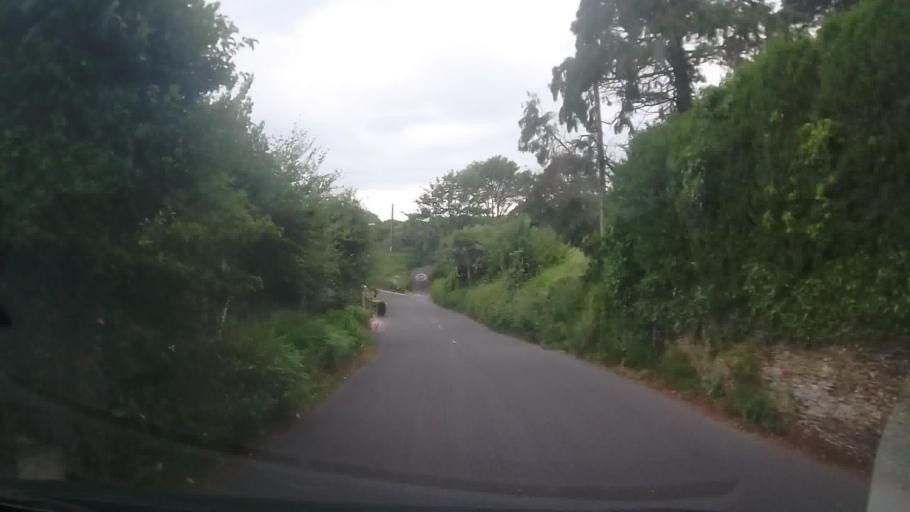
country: GB
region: England
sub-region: Devon
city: Dartmouth
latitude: 50.3128
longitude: -3.6265
